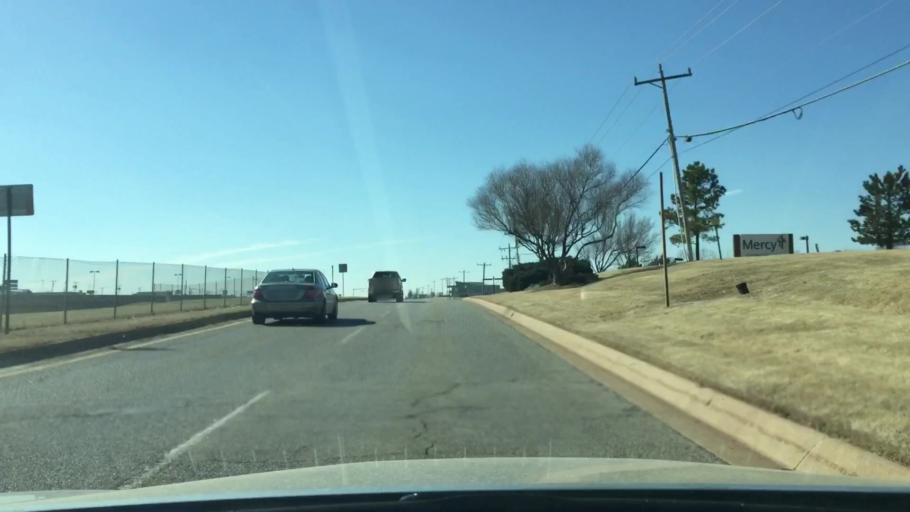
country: US
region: Oklahoma
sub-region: Oklahoma County
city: The Village
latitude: 35.6103
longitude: -97.6116
